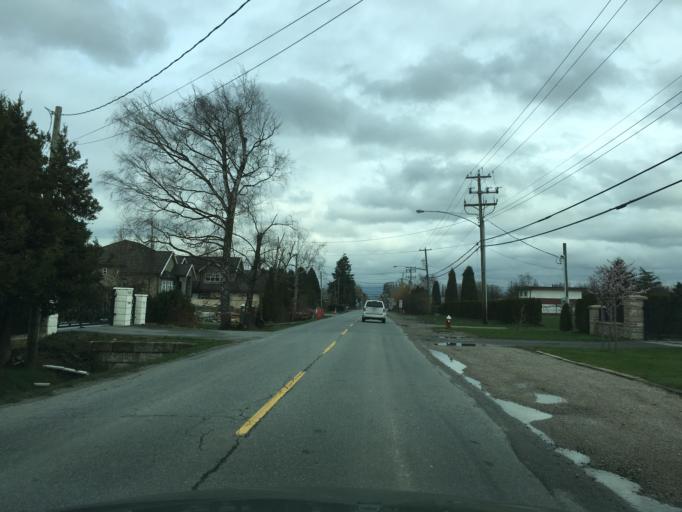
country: CA
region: British Columbia
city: Richmond
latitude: 49.1674
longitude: -123.0692
